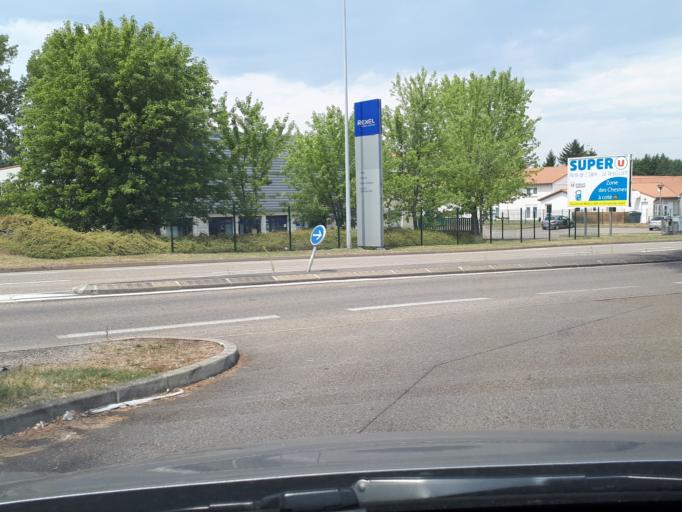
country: FR
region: Rhone-Alpes
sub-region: Departement de l'Isere
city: Domarin
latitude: 45.5918
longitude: 5.2467
